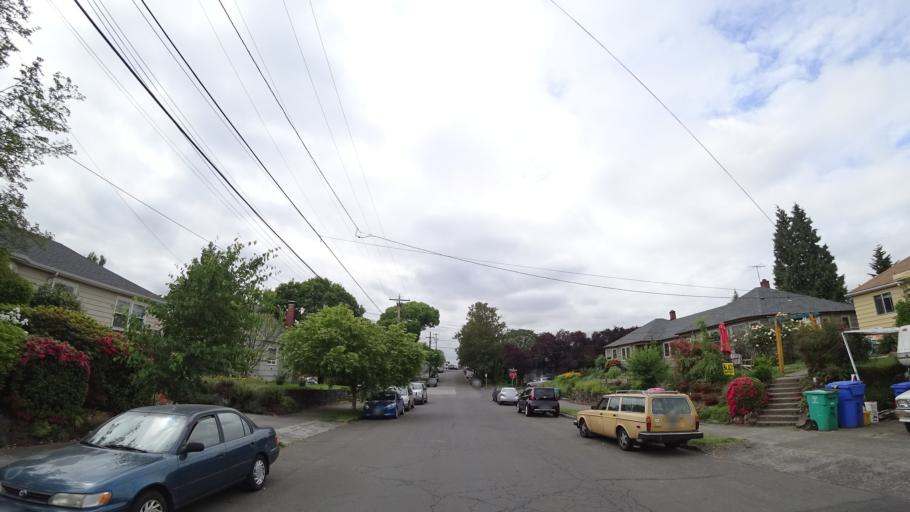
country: US
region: Oregon
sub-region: Multnomah County
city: Portland
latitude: 45.4986
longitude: -122.6356
